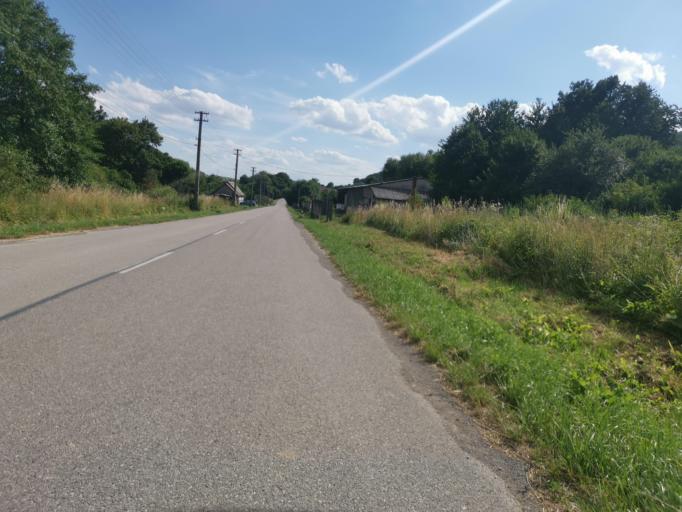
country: CZ
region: South Moravian
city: Knezdub
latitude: 48.7975
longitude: 17.4094
